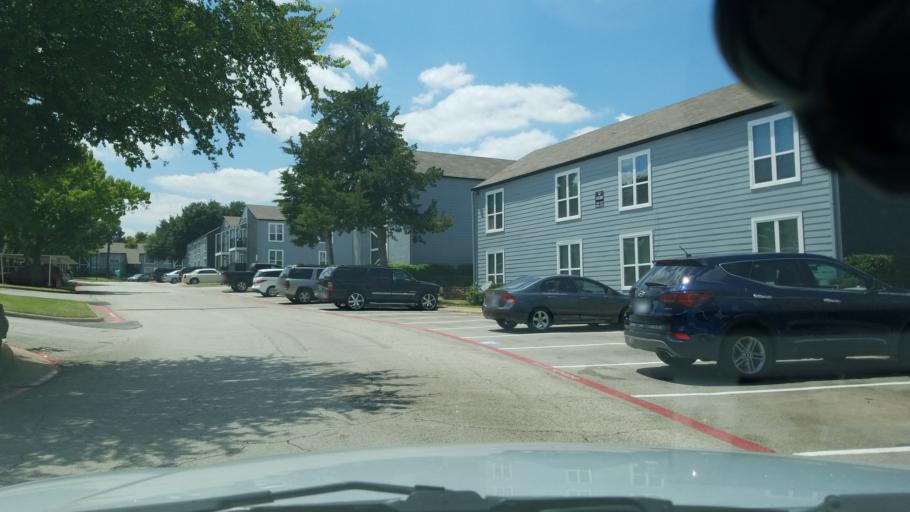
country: US
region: Texas
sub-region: Dallas County
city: Cockrell Hill
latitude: 32.6903
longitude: -96.8623
